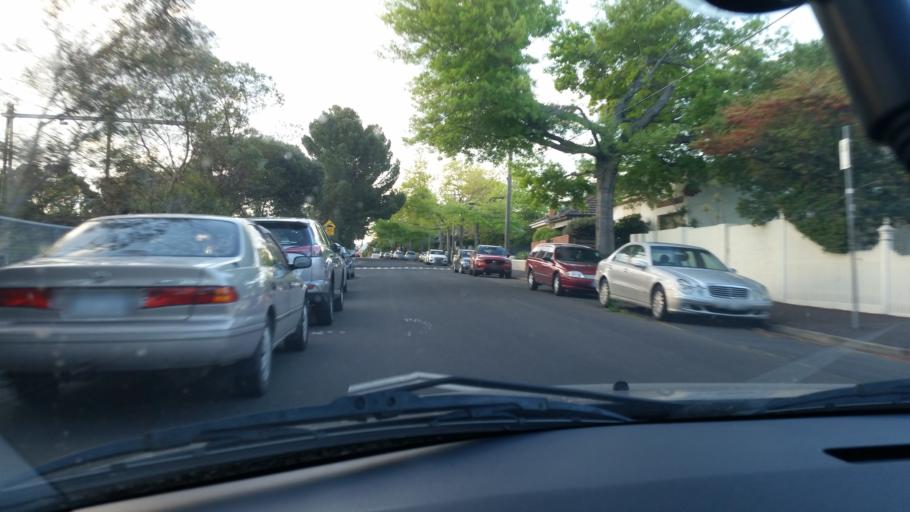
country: AU
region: Victoria
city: Kensington
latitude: -37.7820
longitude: 144.9276
